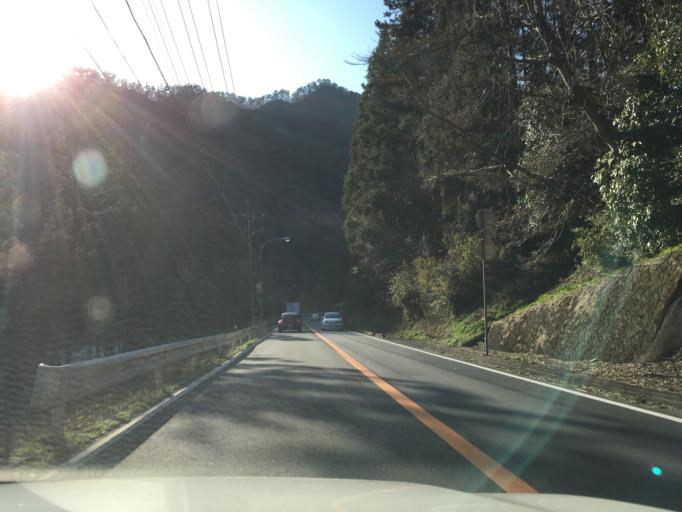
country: JP
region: Ibaraki
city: Daigo
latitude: 36.7358
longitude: 140.3794
